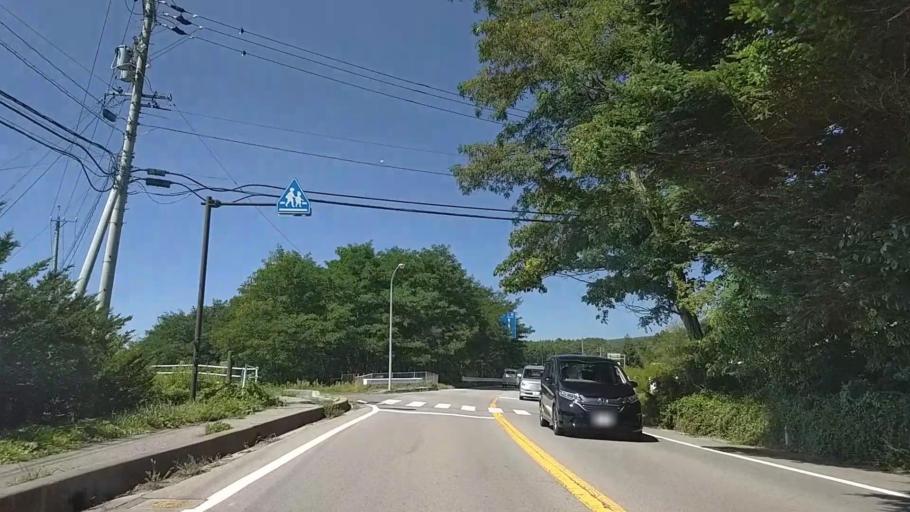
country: JP
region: Nagano
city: Komoro
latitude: 36.3375
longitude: 138.5055
